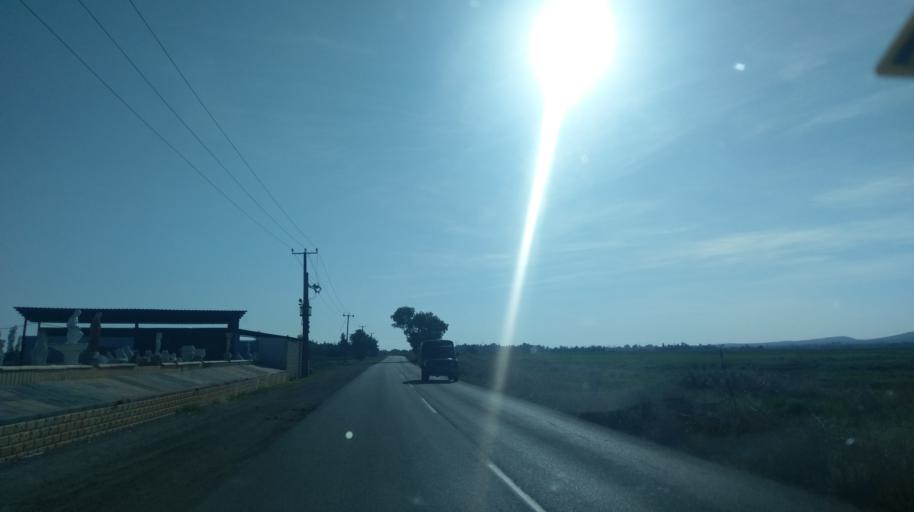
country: CY
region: Larnaka
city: Pergamos
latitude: 35.0600
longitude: 33.7128
